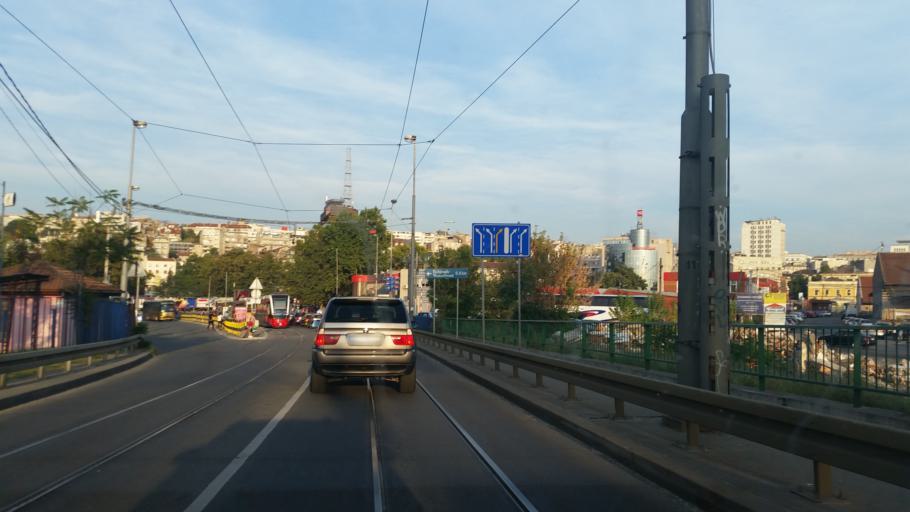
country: RS
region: Central Serbia
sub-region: Belgrade
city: Stari Grad
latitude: 44.8107
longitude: 20.4523
